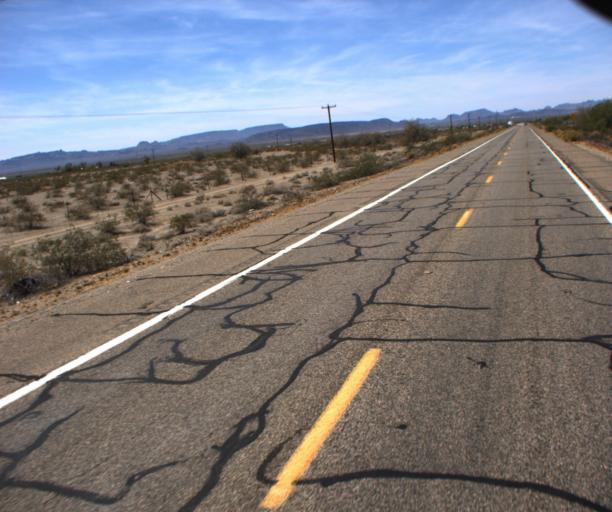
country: US
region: Arizona
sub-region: La Paz County
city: Salome
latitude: 33.7190
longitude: -113.7597
